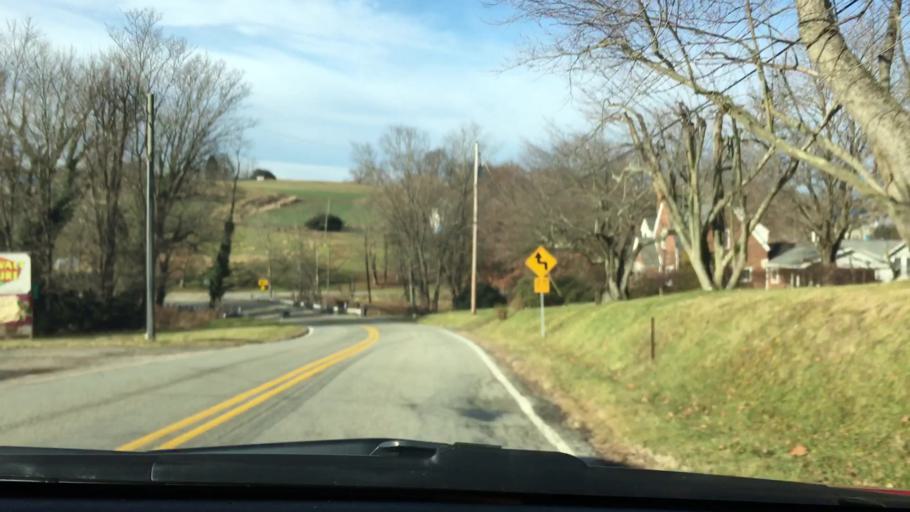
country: US
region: Pennsylvania
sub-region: Westmoreland County
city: Collinsburg
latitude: 40.2390
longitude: -79.6979
